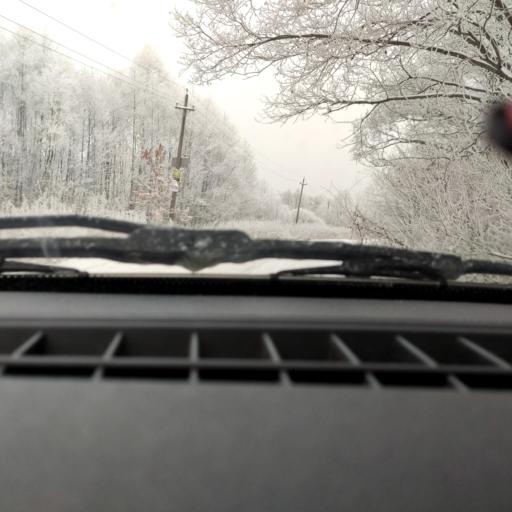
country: RU
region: Bashkortostan
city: Ufa
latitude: 54.7111
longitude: 56.1275
